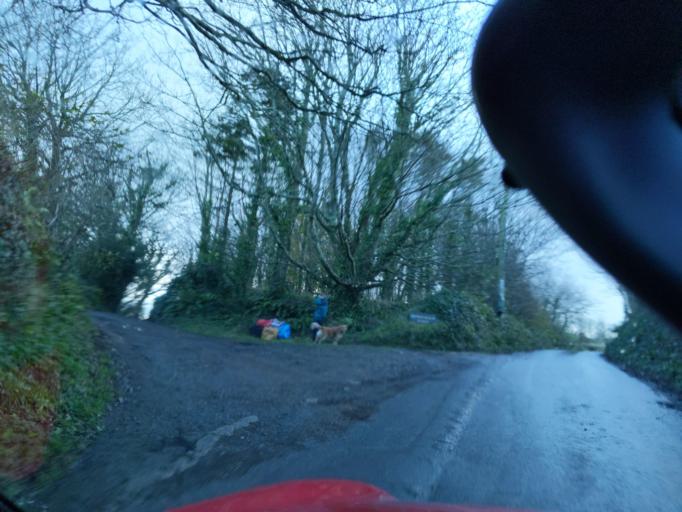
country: GB
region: England
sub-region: Cornwall
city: Looe
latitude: 50.3428
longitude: -4.4801
